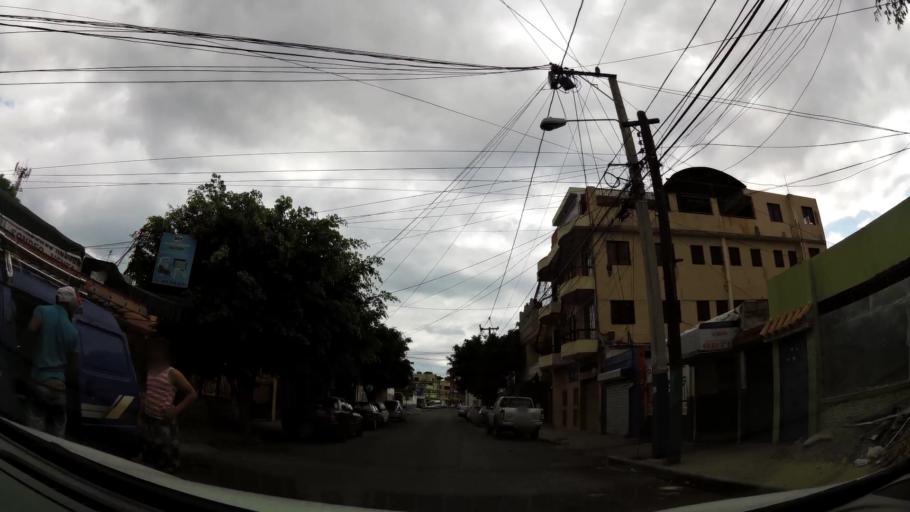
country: DO
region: Nacional
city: San Carlos
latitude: 18.4856
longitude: -69.9158
